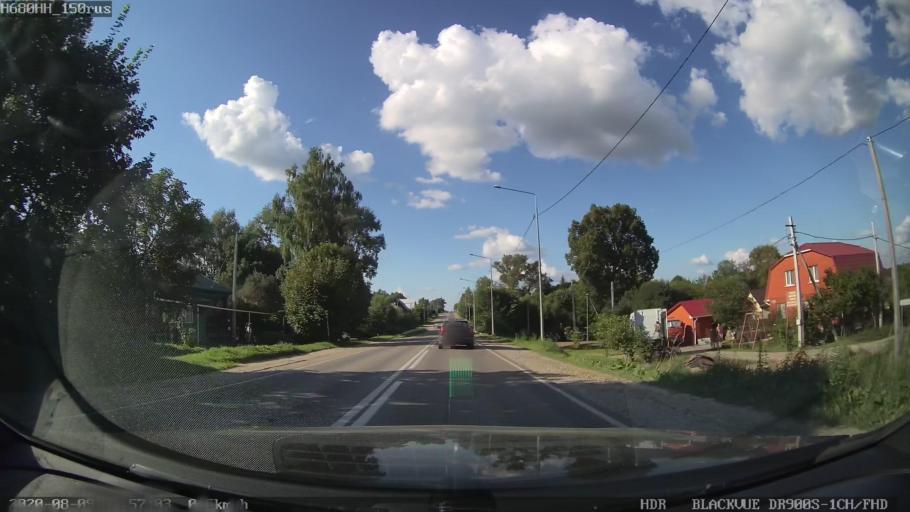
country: RU
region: Tula
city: Zaokskiy
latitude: 54.8001
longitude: 37.4320
